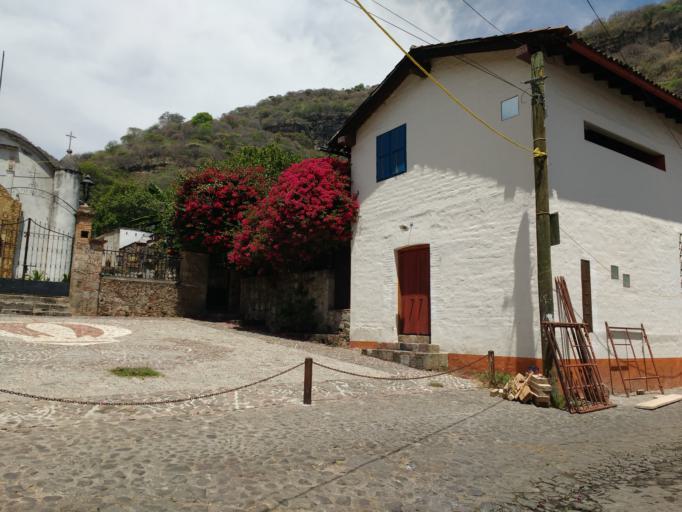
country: MX
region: Mexico
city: Malinalco
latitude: 18.9515
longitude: -99.5005
